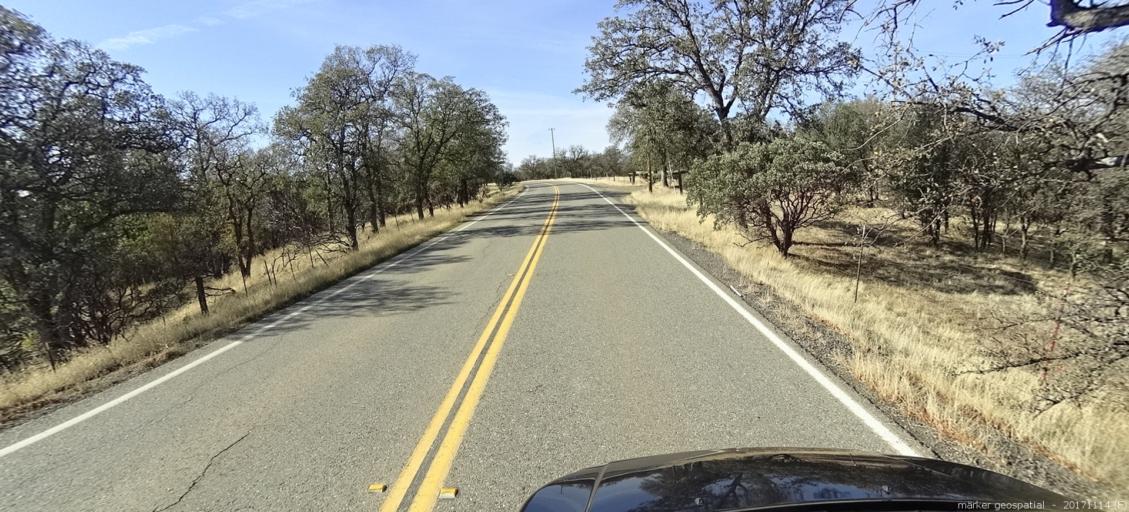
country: US
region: California
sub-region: Shasta County
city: Anderson
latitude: 40.4230
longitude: -122.3337
